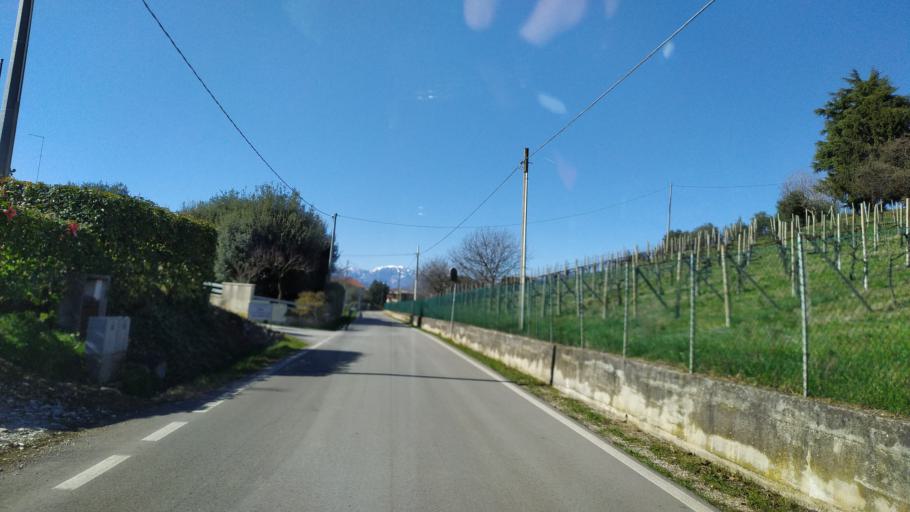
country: IT
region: Veneto
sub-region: Provincia di Vicenza
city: Breganze
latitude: 45.7019
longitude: 11.5771
